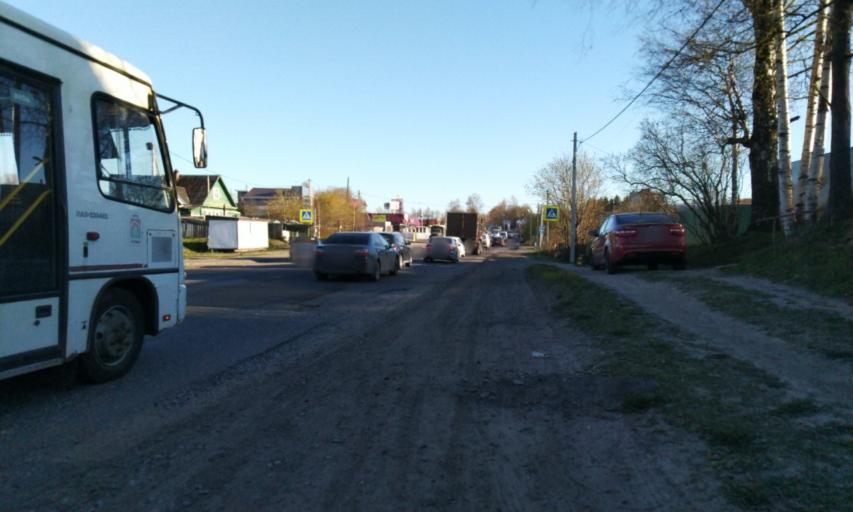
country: RU
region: Leningrad
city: Toksovo
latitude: 60.1146
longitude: 30.5029
